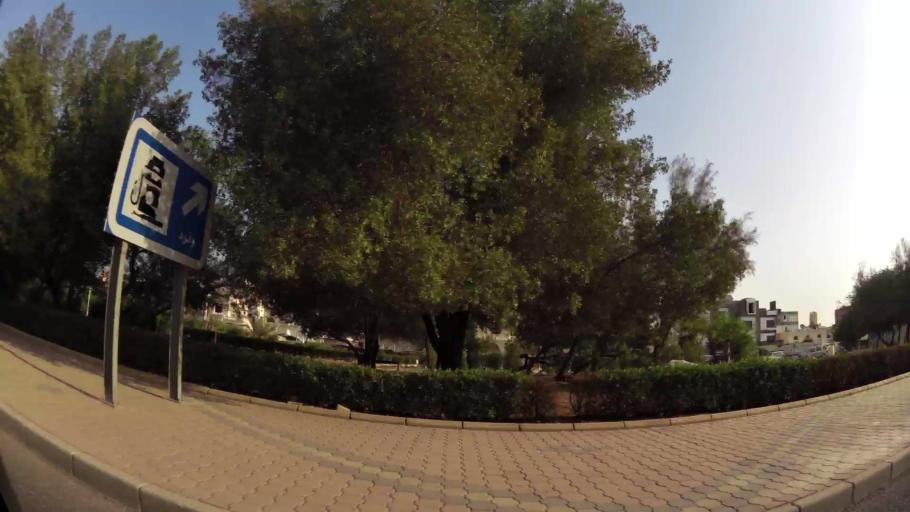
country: KW
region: Muhafazat Hawalli
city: Hawalli
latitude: 29.3477
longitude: 48.0200
